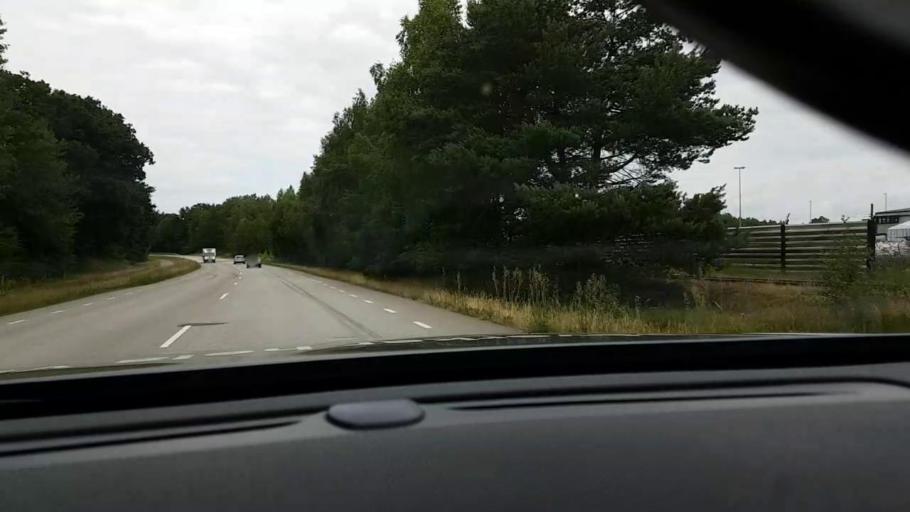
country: SE
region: Skane
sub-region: Hassleholms Kommun
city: Hassleholm
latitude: 56.1621
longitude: 13.8040
